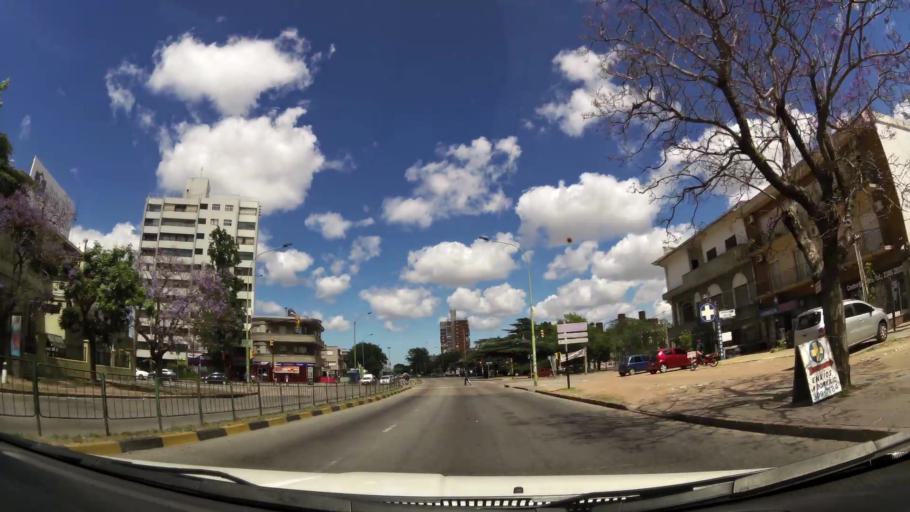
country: UY
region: Montevideo
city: Montevideo
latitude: -34.8733
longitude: -56.2016
